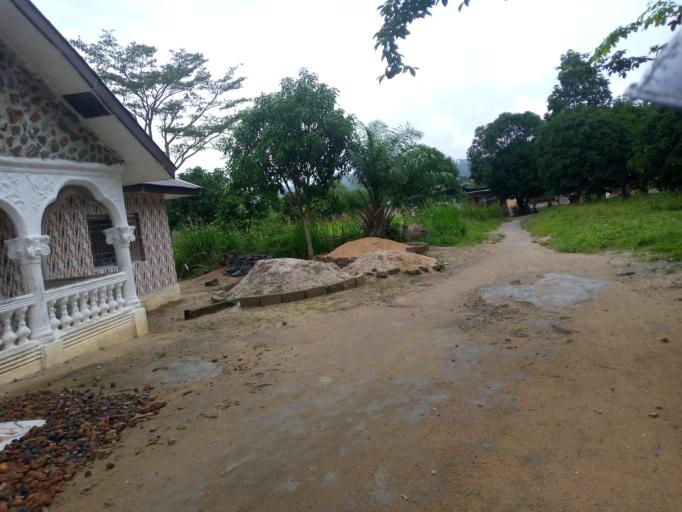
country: SL
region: Eastern Province
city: Kenema
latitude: 7.8417
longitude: -11.2048
